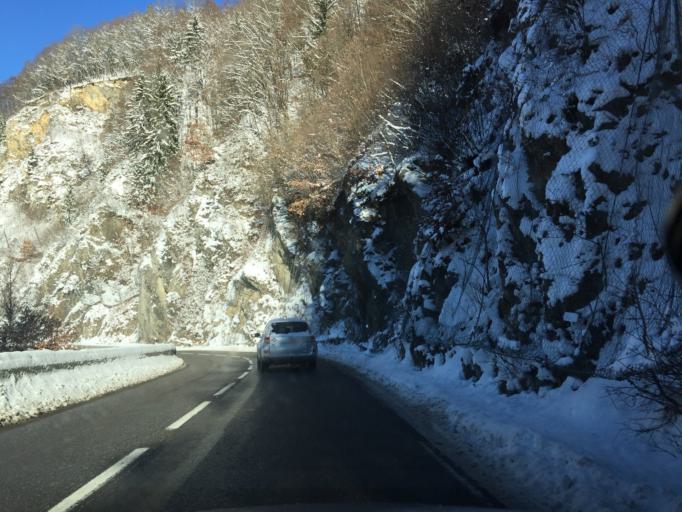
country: FR
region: Rhone-Alpes
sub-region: Departement de la Haute-Savoie
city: Saint-Paul-en-Chablais
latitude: 46.3332
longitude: 6.6581
